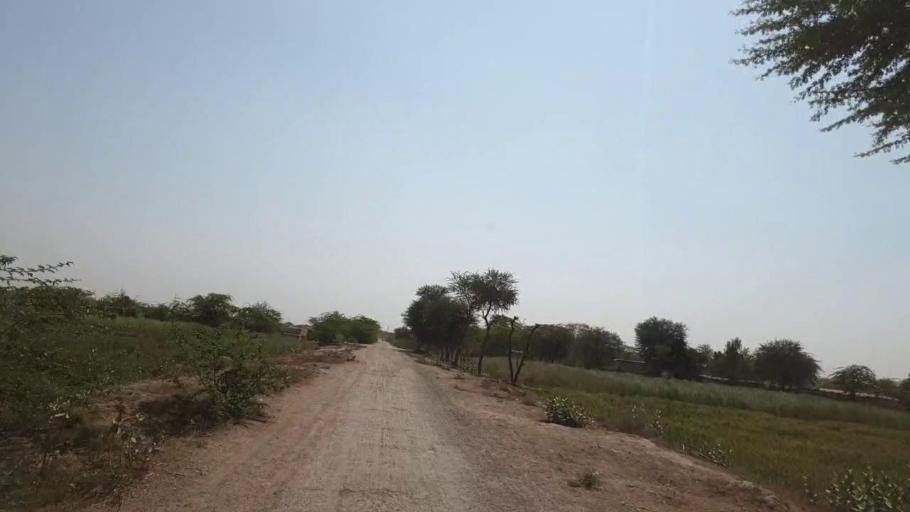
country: PK
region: Sindh
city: Kunri
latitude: 25.0865
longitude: 69.5322
